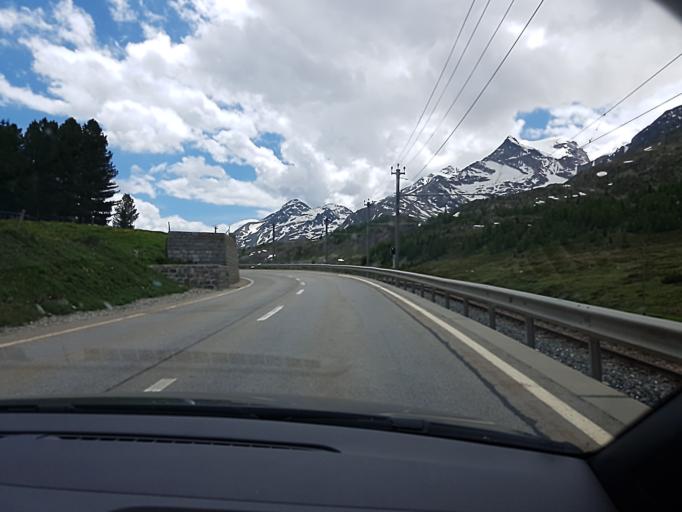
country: CH
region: Grisons
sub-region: Maloja District
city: Pontresina
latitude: 46.4413
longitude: 9.9860
